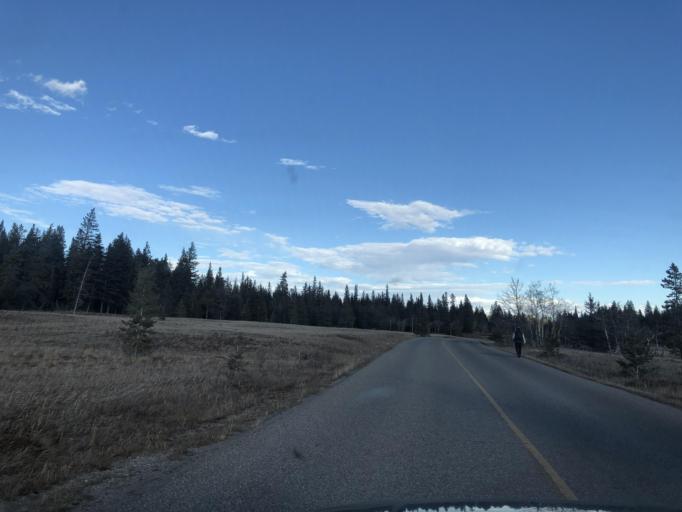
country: CA
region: Alberta
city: Canmore
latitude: 51.0791
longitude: -115.0861
